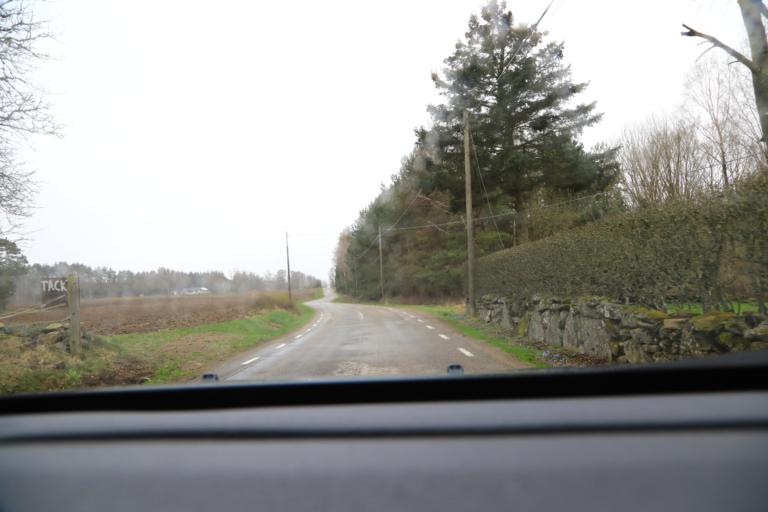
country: SE
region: Halland
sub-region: Kungsbacka Kommun
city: Frillesas
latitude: 57.2780
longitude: 12.2021
